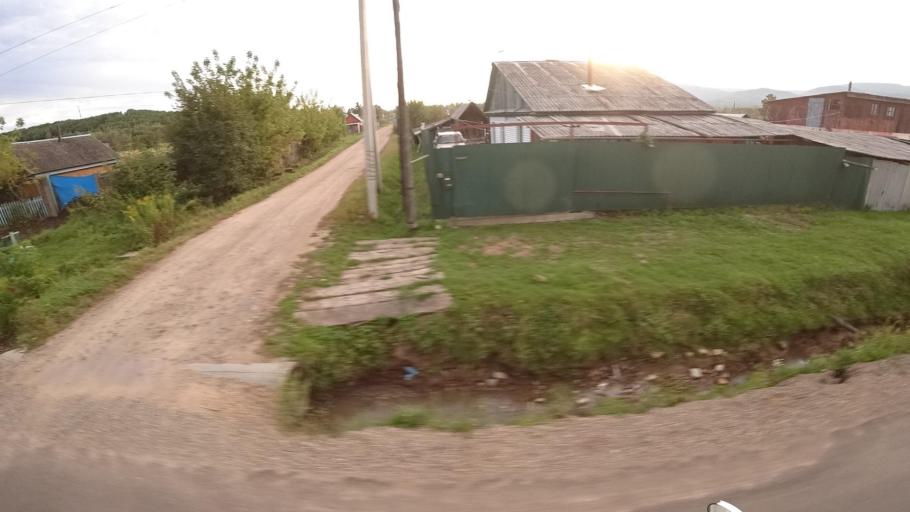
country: RU
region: Primorskiy
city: Yakovlevka
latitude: 44.4229
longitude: 133.4662
